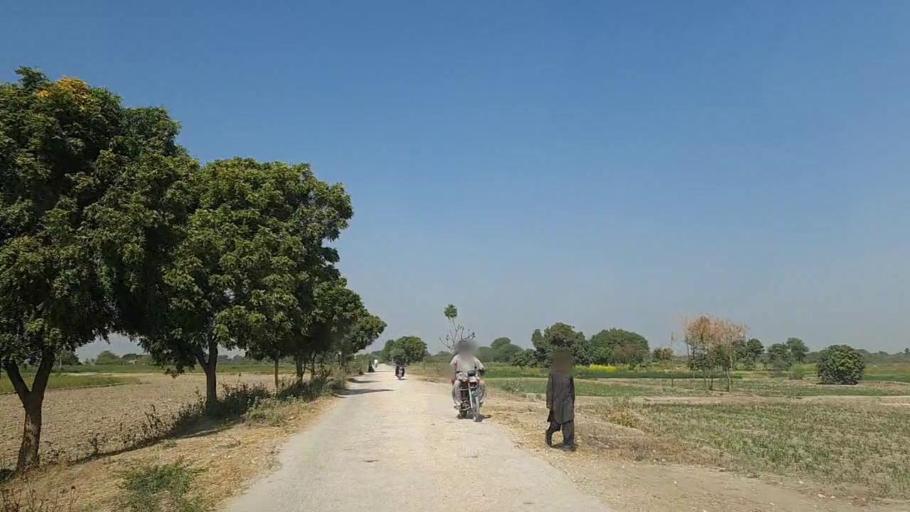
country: PK
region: Sindh
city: Naukot
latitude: 24.8689
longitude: 69.4037
